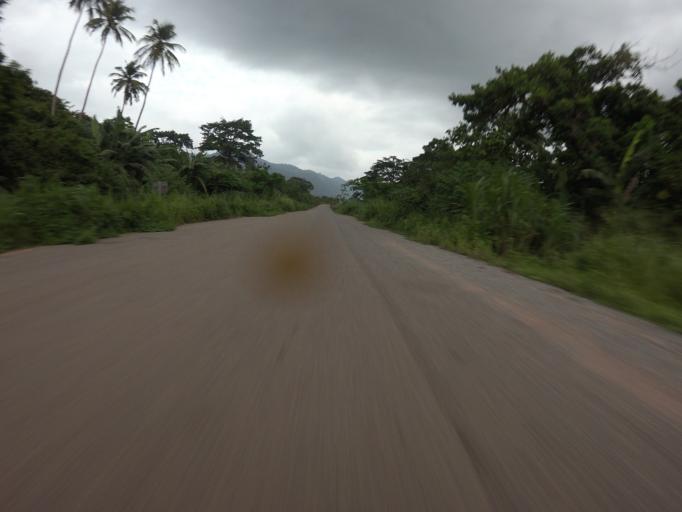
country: GH
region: Volta
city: Ho
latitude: 6.7828
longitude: 0.3658
